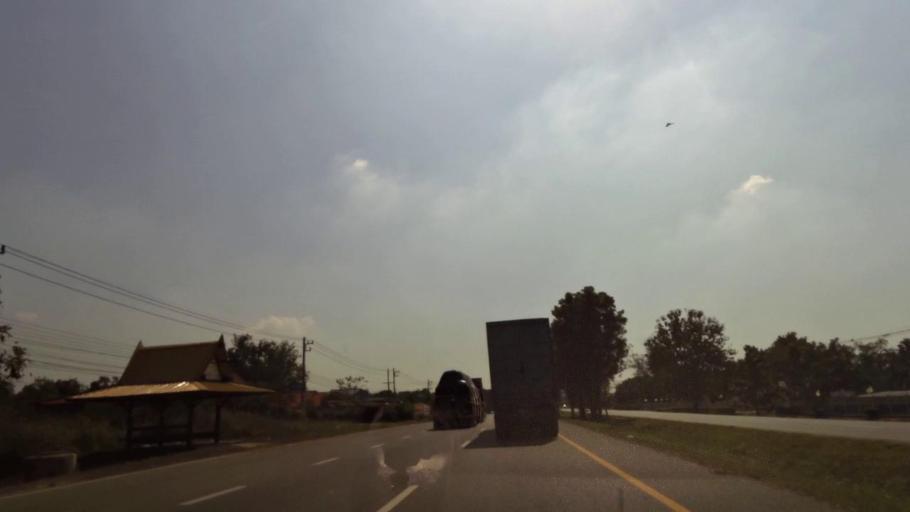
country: TH
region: Phichit
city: Bueng Na Rang
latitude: 16.1371
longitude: 100.1255
